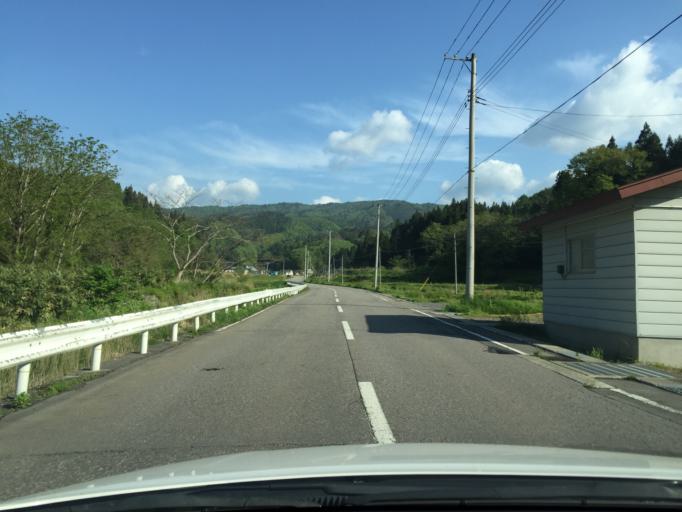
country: JP
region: Fukushima
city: Kitakata
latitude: 37.6589
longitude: 139.7567
